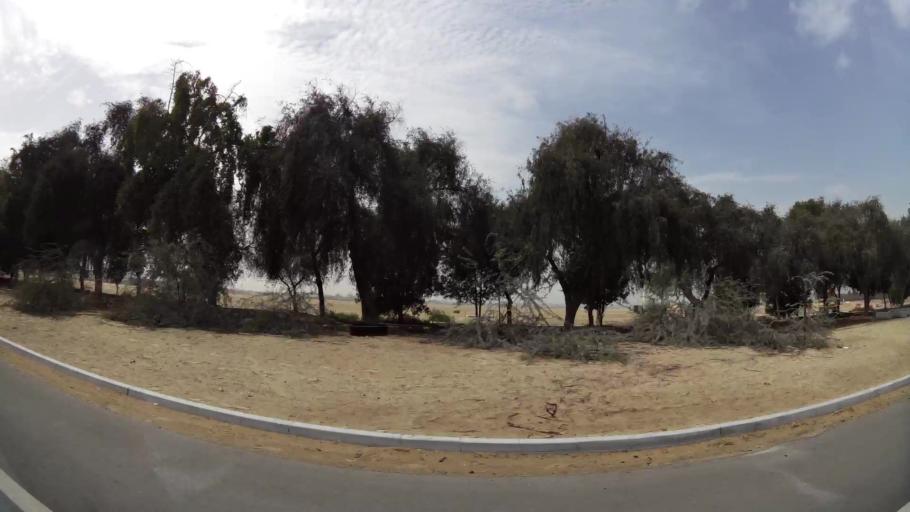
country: AE
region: Abu Dhabi
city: Abu Dhabi
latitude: 24.3919
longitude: 54.5220
